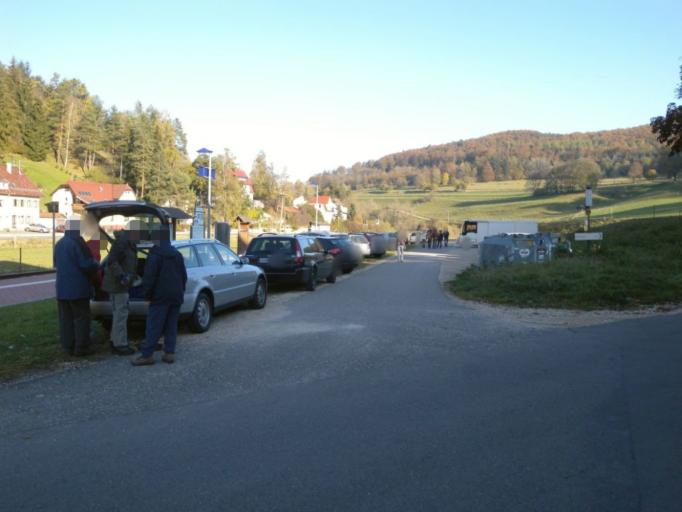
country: DE
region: Baden-Wuerttemberg
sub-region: Tuebingen Region
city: Gomadingen
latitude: 48.3995
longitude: 9.3697
